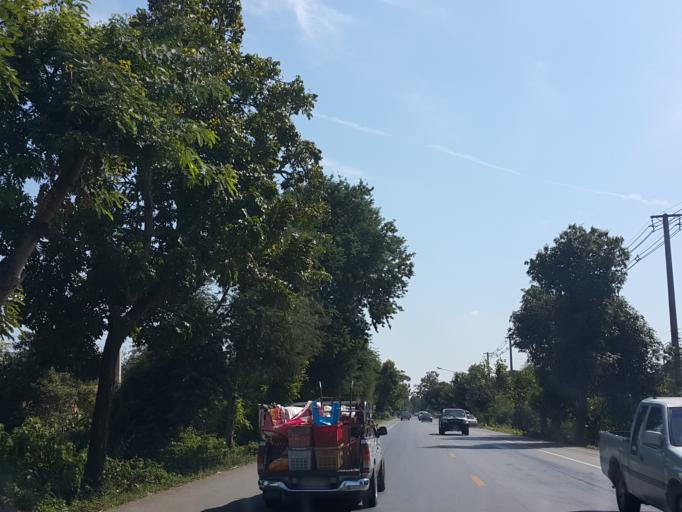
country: TH
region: Sukhothai
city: Sawankhalok
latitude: 17.2583
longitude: 99.8508
